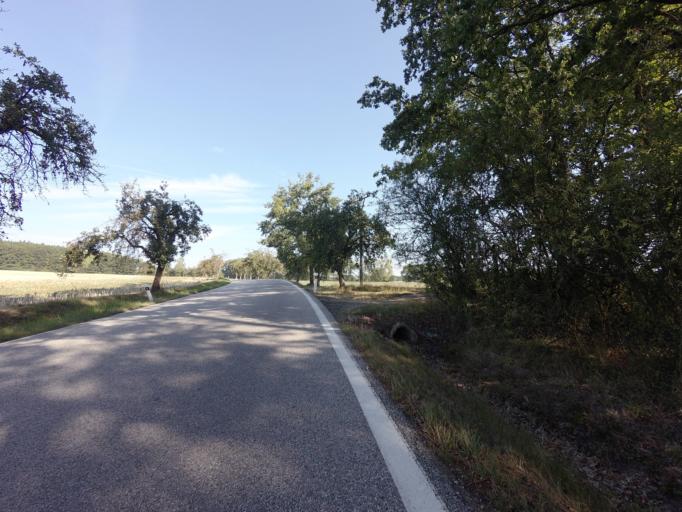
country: CZ
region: Jihocesky
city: Tyn nad Vltavou
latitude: 49.2567
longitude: 14.4172
